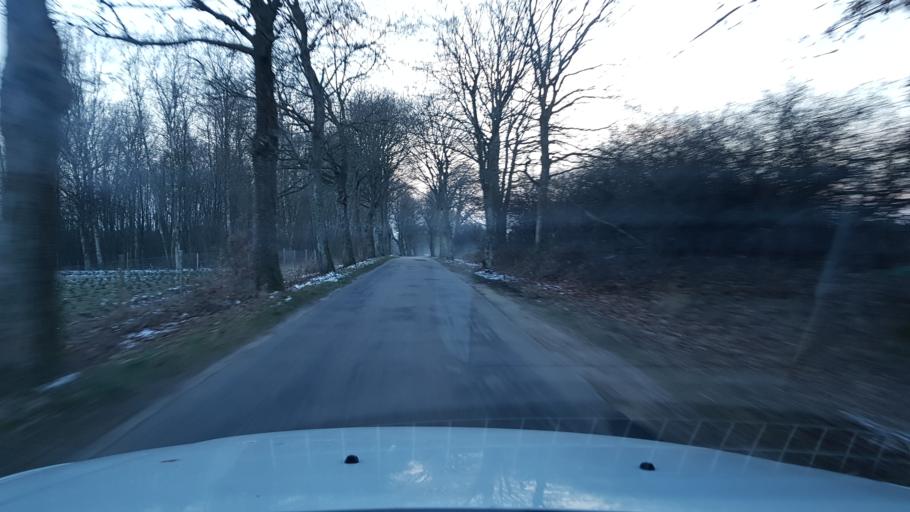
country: PL
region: West Pomeranian Voivodeship
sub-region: Powiat bialogardzki
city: Karlino
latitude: 54.0154
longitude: 15.8459
